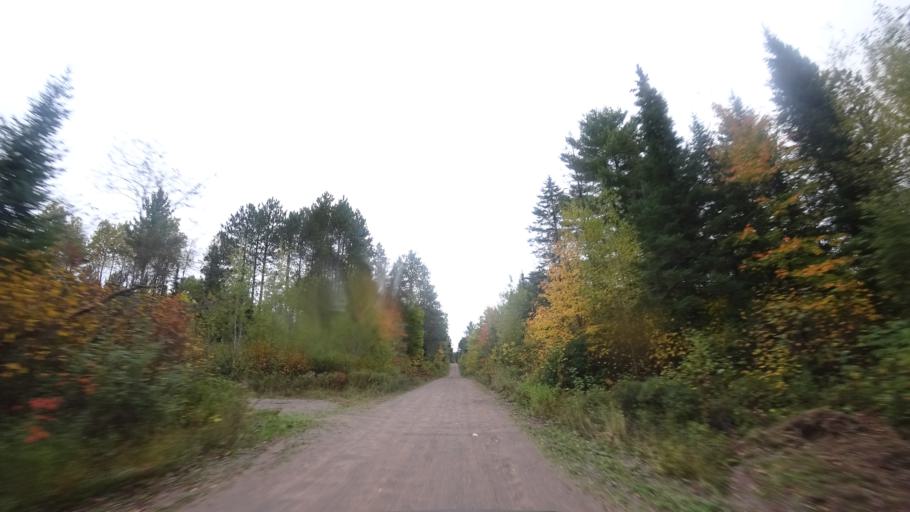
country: US
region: Wisconsin
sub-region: Sawyer County
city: Little Round Lake
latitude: 46.0852
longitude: -90.9819
